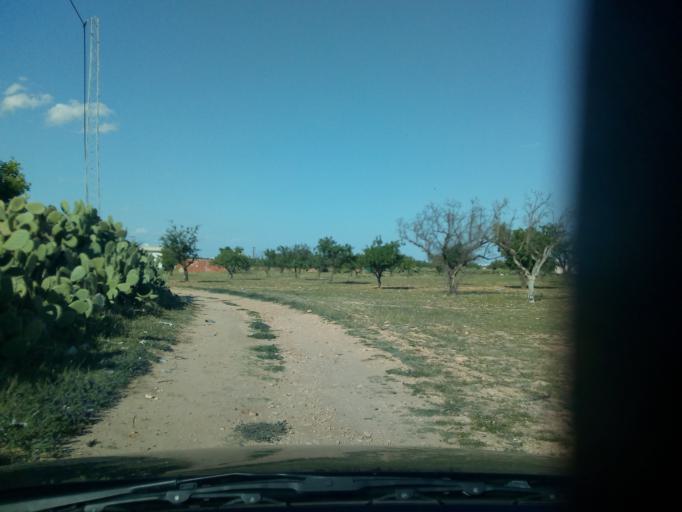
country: TN
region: Safaqis
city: Sfax
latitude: 34.7290
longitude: 10.6122
